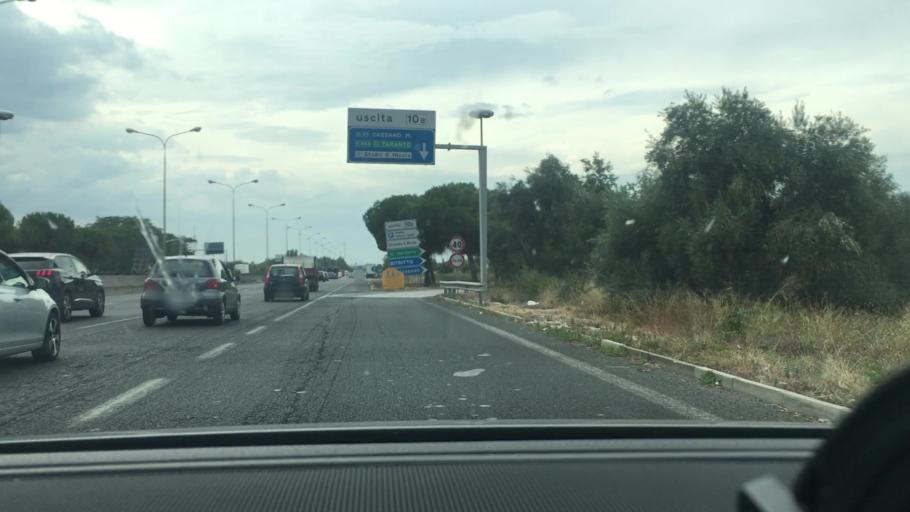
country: IT
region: Apulia
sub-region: Provincia di Bari
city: Bari
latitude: 41.0939
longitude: 16.8393
